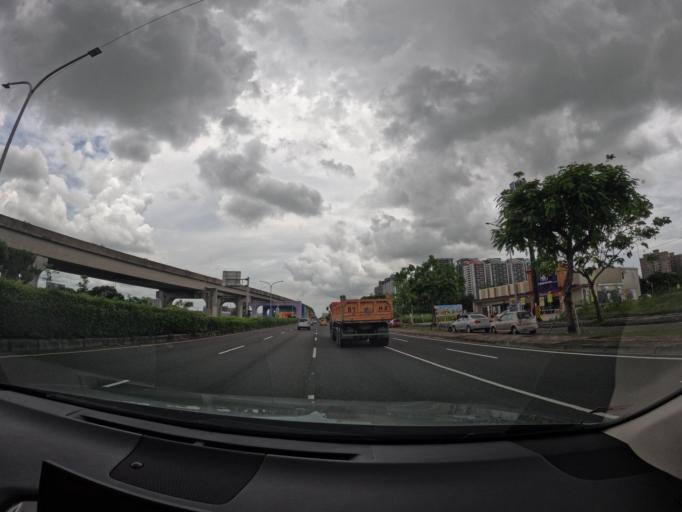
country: TW
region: Taiwan
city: Fengshan
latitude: 22.7423
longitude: 120.3170
